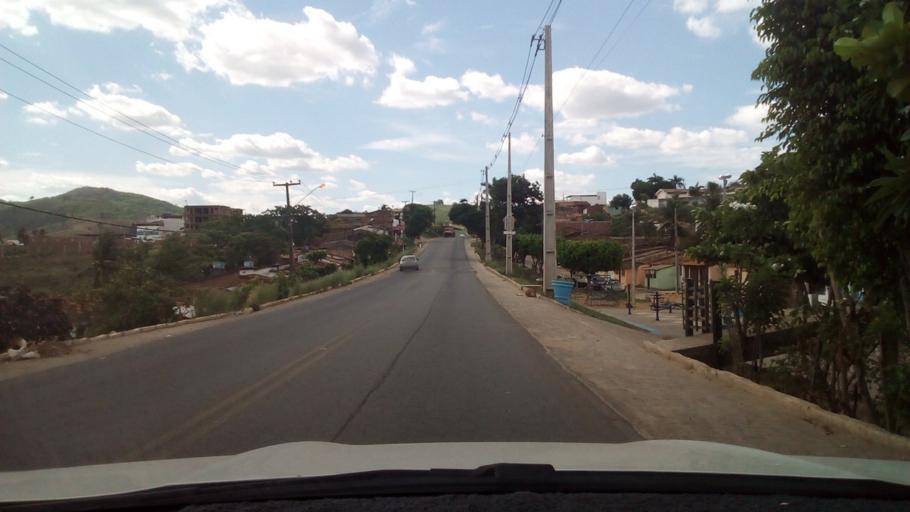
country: BR
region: Paraiba
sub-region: Guarabira
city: Guarabira
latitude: -6.8651
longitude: -35.4928
